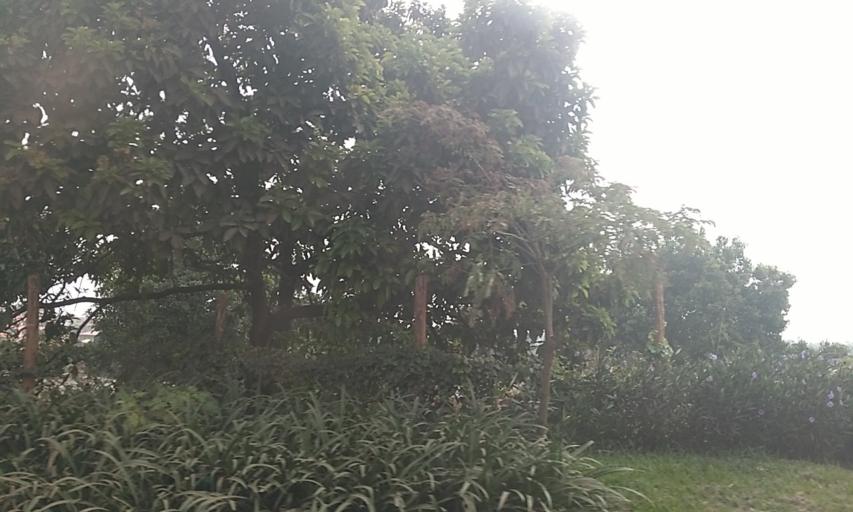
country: UG
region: Central Region
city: Kampala Central Division
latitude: 0.3034
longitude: 32.5582
